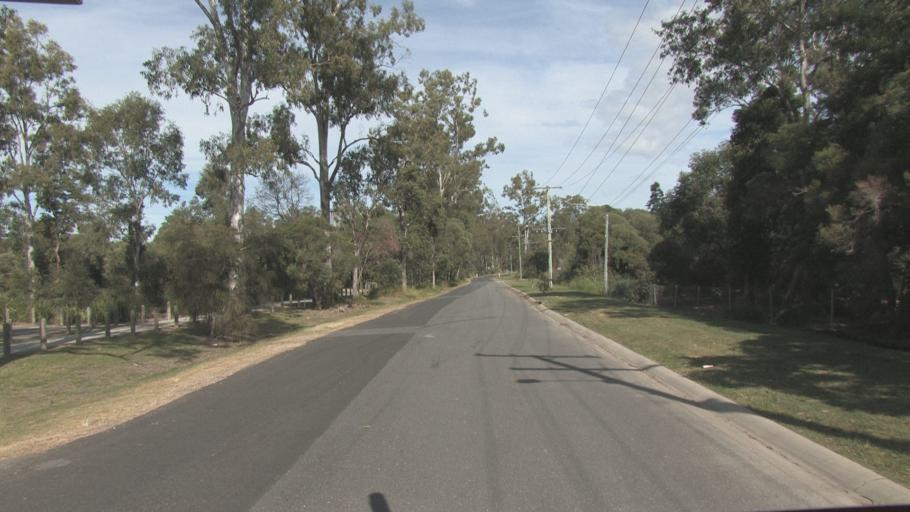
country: AU
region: Queensland
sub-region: Logan
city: Woodridge
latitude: -27.6633
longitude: 153.0868
